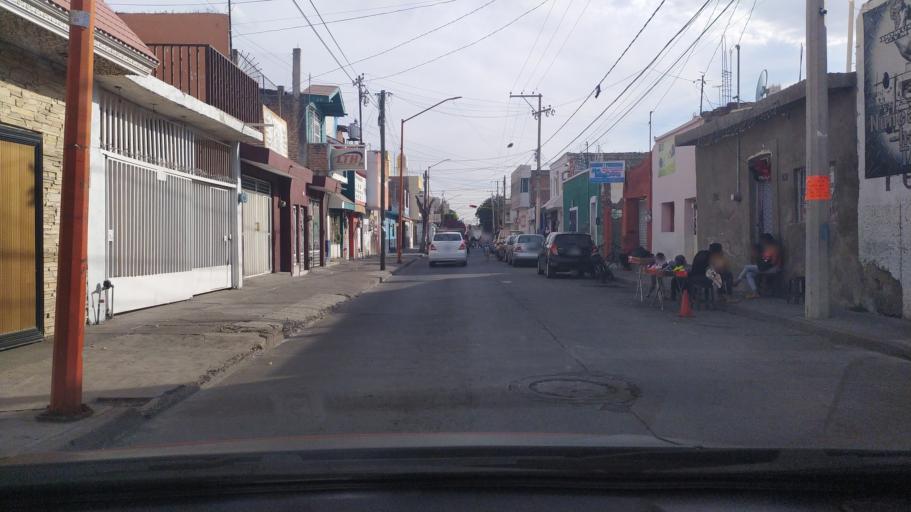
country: MX
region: Guanajuato
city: San Francisco del Rincon
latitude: 21.0169
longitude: -101.8535
